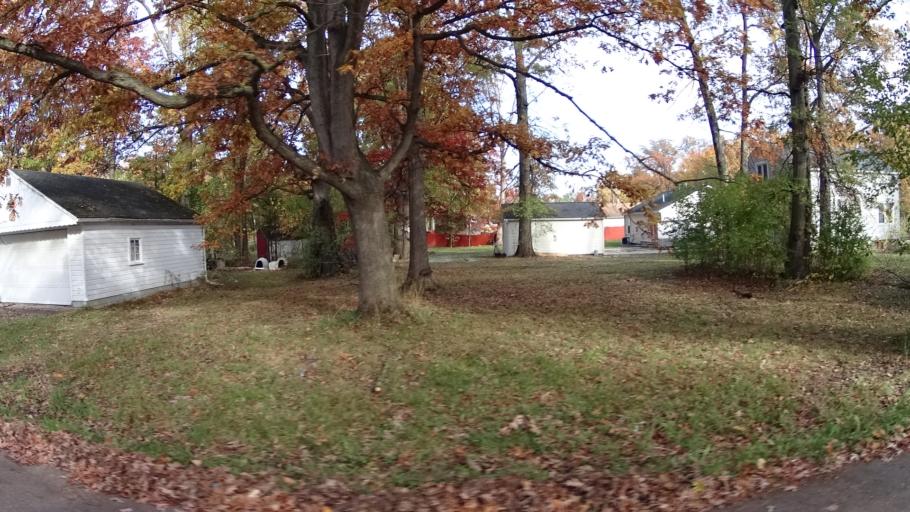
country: US
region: Ohio
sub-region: Lorain County
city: Sheffield
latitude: 41.4350
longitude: -82.1382
